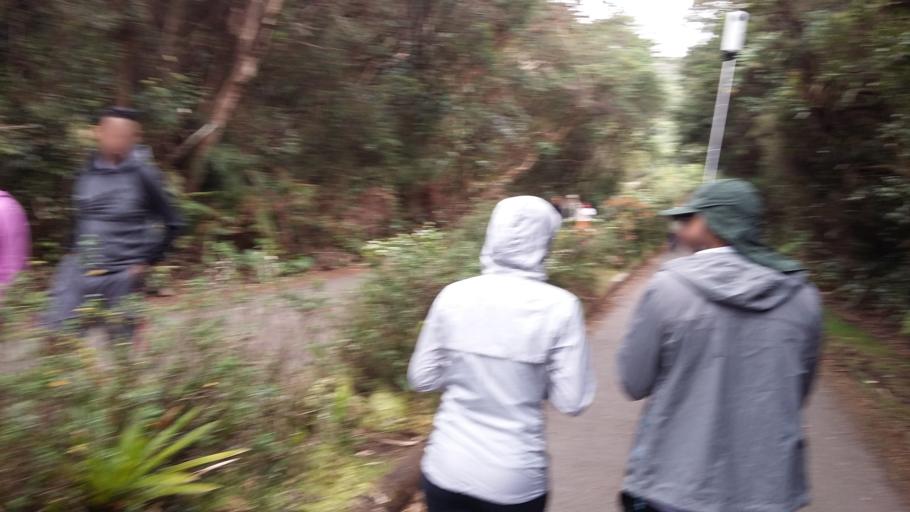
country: CR
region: Alajuela
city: Rio Segundo
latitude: 10.1879
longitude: -84.2338
